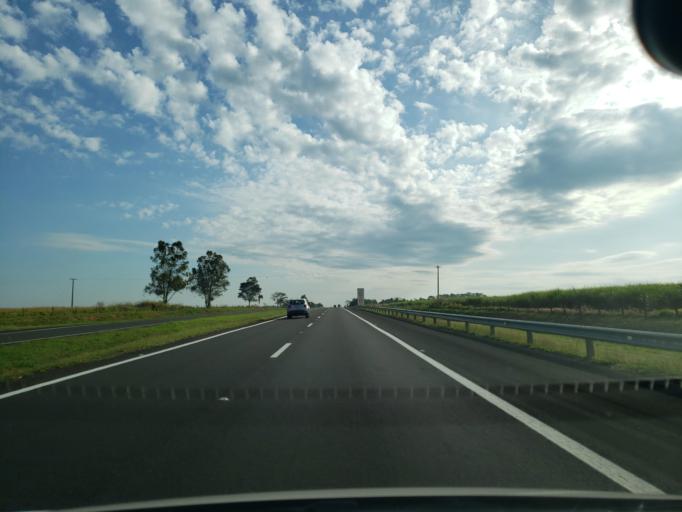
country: BR
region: Sao Paulo
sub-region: Guararapes
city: Guararapes
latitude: -21.2031
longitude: -50.6035
